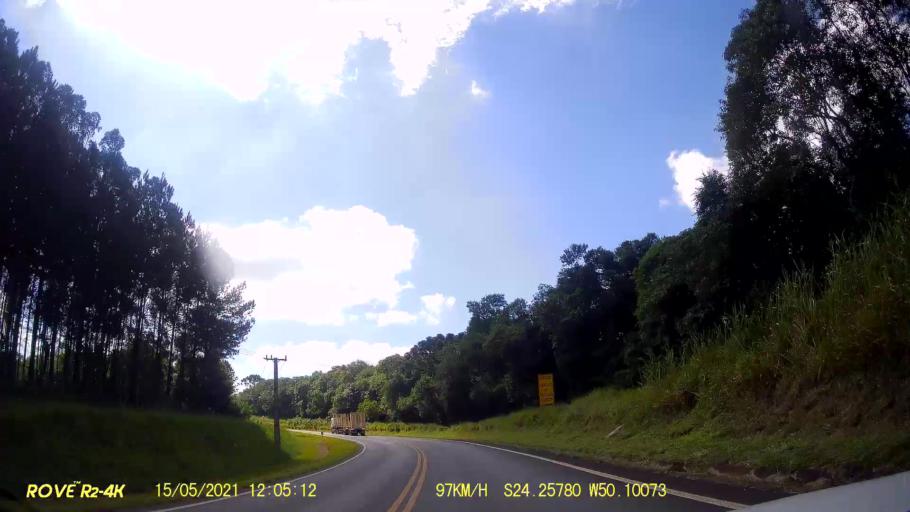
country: BR
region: Parana
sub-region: Pirai Do Sul
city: Pirai do Sul
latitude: -24.2577
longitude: -50.1008
